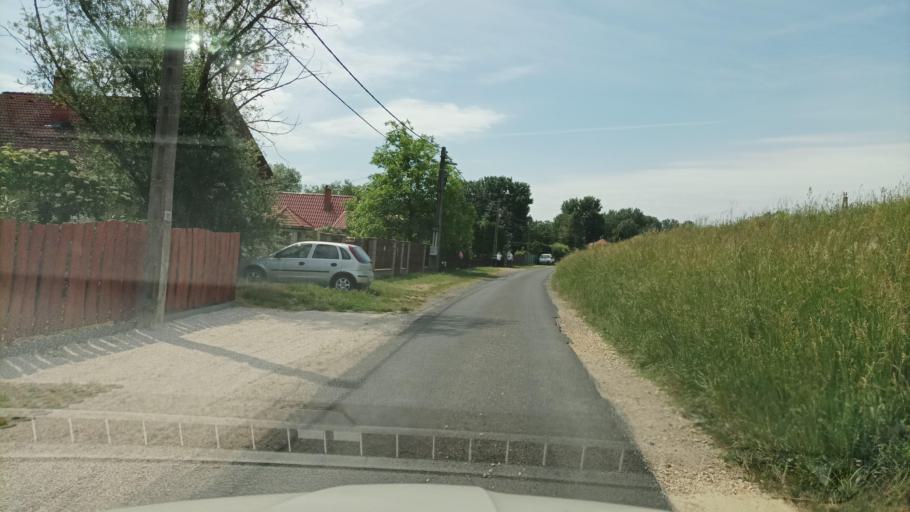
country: HU
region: Pest
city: Domsod
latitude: 47.1047
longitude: 18.9979
